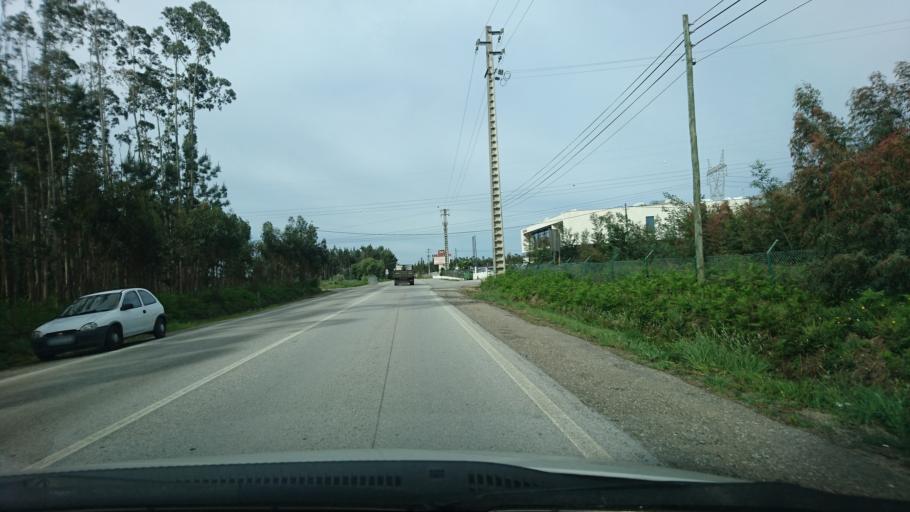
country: PT
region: Aveiro
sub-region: Albergaria-A-Velha
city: Albergaria-a-Velha
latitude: 40.7017
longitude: -8.5000
